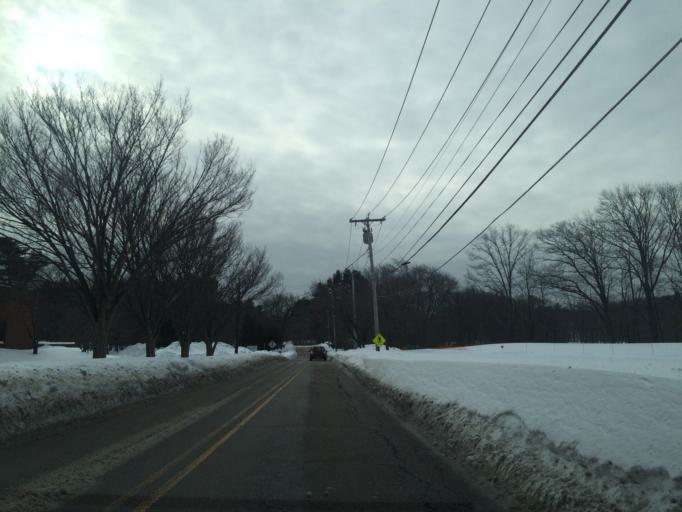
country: US
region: Massachusetts
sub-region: Norfolk County
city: Wellesley
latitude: 42.3321
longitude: -71.2686
